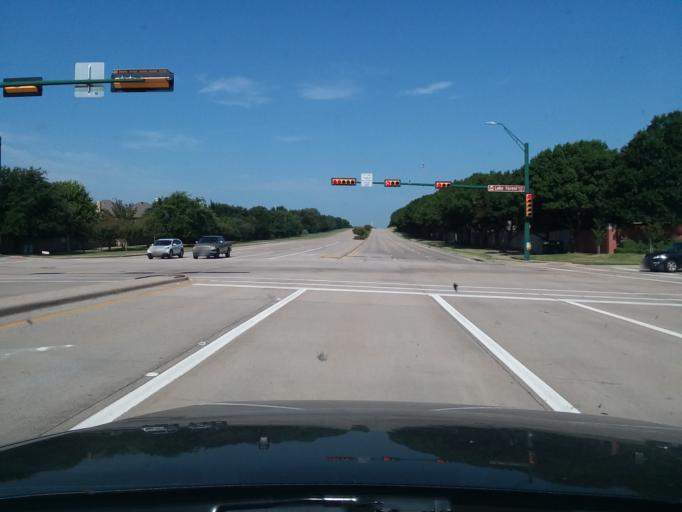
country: US
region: Texas
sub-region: Denton County
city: Flower Mound
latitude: 33.0138
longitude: -97.0612
